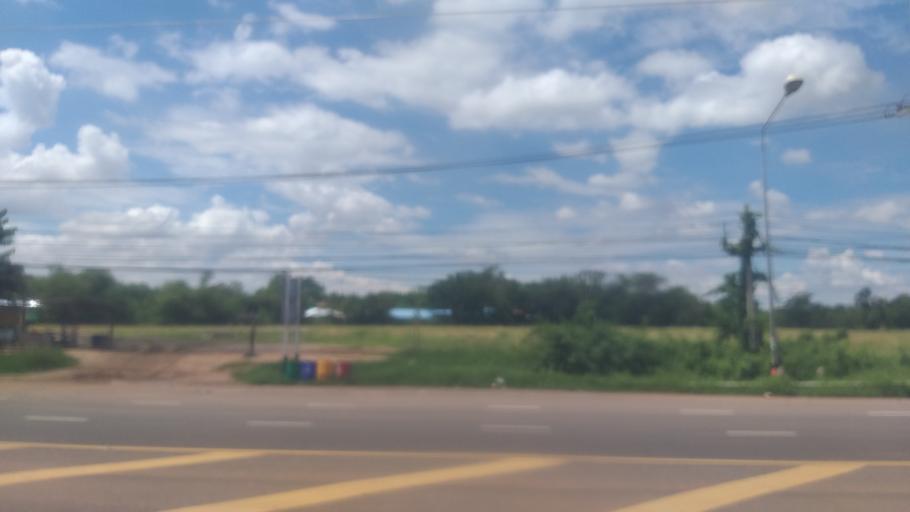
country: TH
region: Nakhon Ratchasima
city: Phra Thong Kham
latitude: 15.3093
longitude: 101.9679
